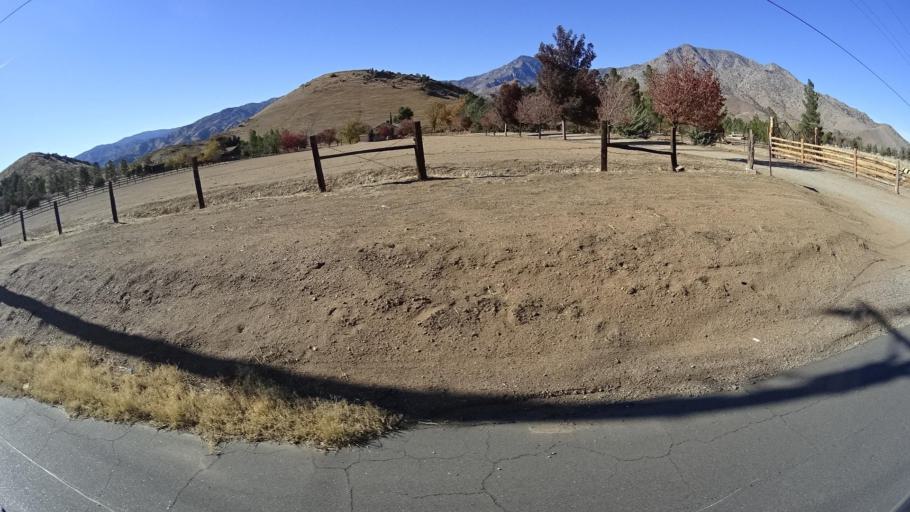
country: US
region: California
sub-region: Kern County
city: Wofford Heights
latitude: 35.7022
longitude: -118.4230
